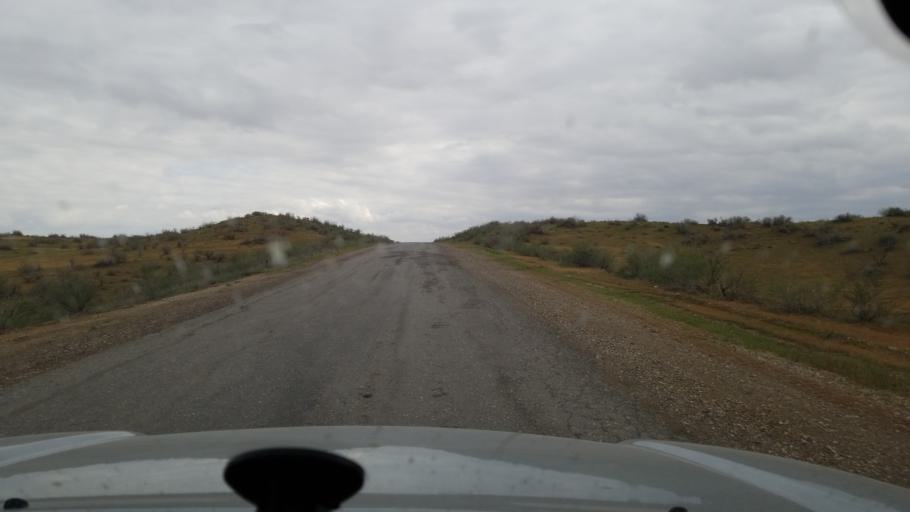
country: TM
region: Mary
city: Serhetabat
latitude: 36.0963
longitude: 62.6111
